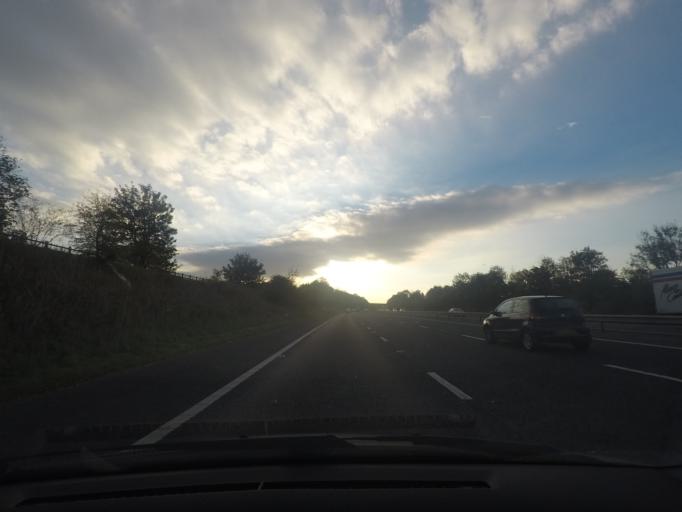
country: GB
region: England
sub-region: North Lincolnshire
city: Brigg
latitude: 53.5516
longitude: -0.5181
